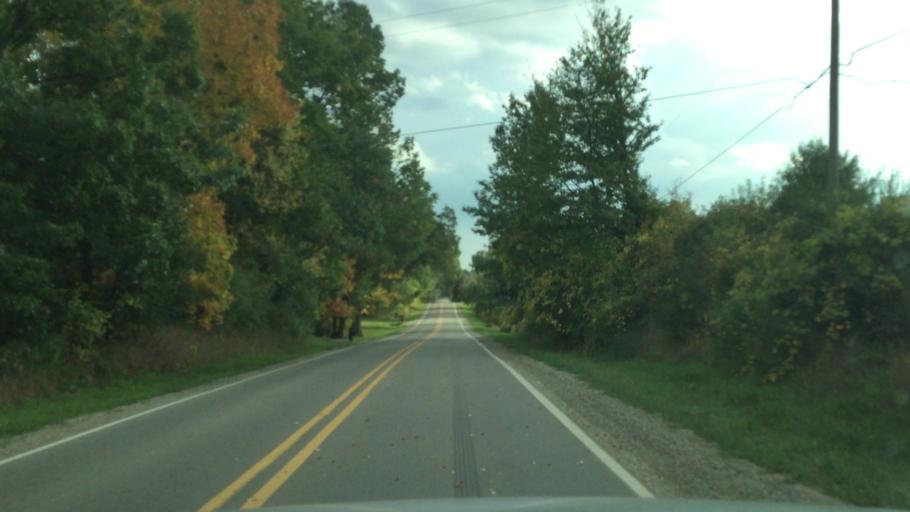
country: US
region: Michigan
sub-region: Genesee County
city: Fenton
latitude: 42.6854
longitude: -83.7026
